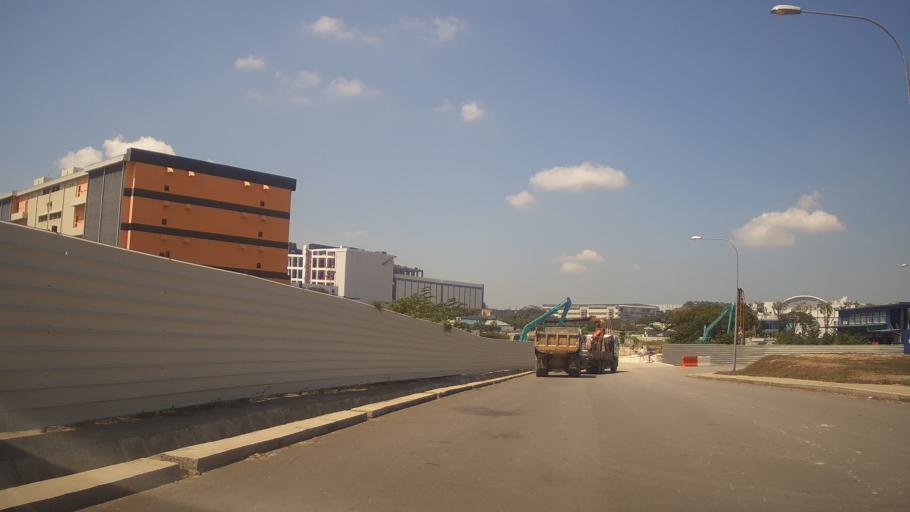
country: SG
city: Singapore
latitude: 1.3228
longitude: 103.7232
